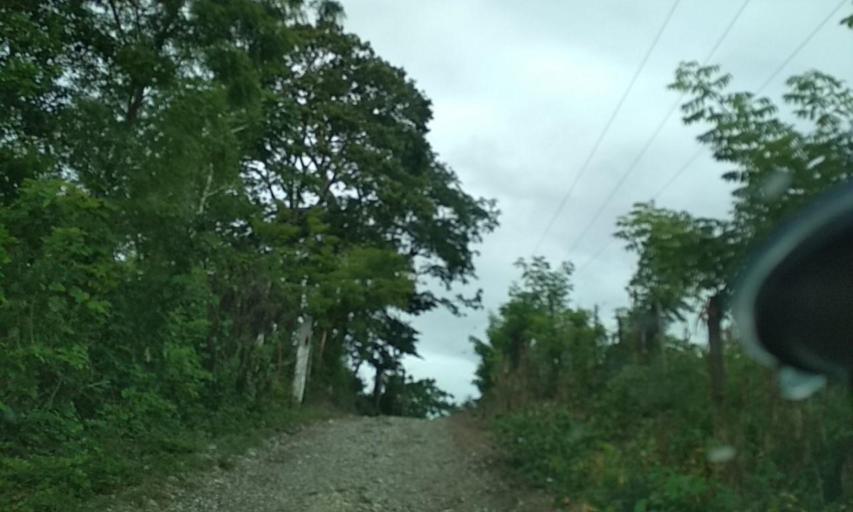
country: MX
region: Veracruz
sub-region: Papantla
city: Residencial Tajin
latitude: 20.6107
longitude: -97.3536
